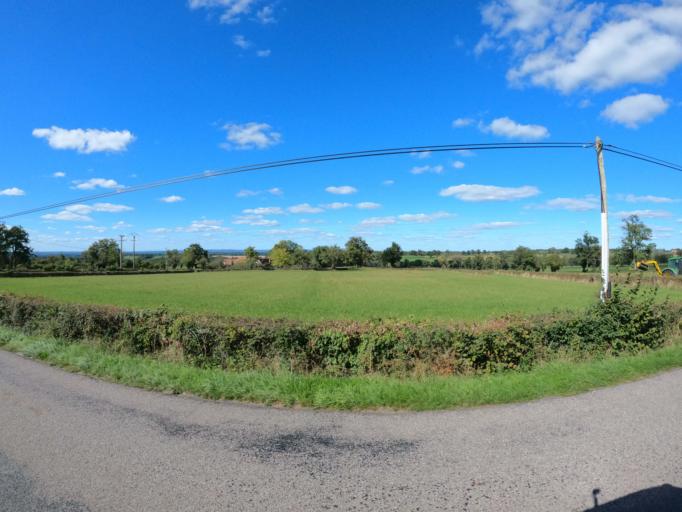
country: FR
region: Auvergne
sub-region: Departement de l'Allier
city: Buxieres-les-Mines
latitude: 46.4041
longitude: 2.9277
